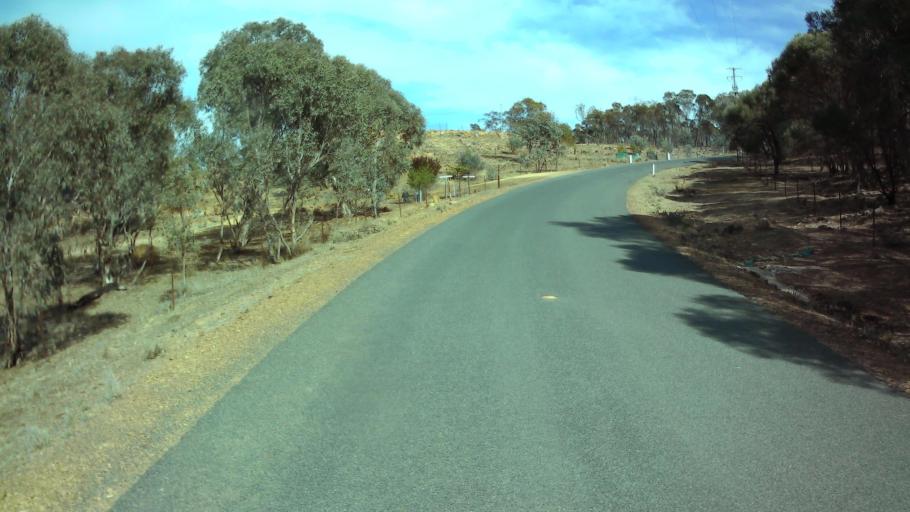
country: AU
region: New South Wales
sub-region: Weddin
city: Grenfell
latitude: -33.8794
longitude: 148.1935
